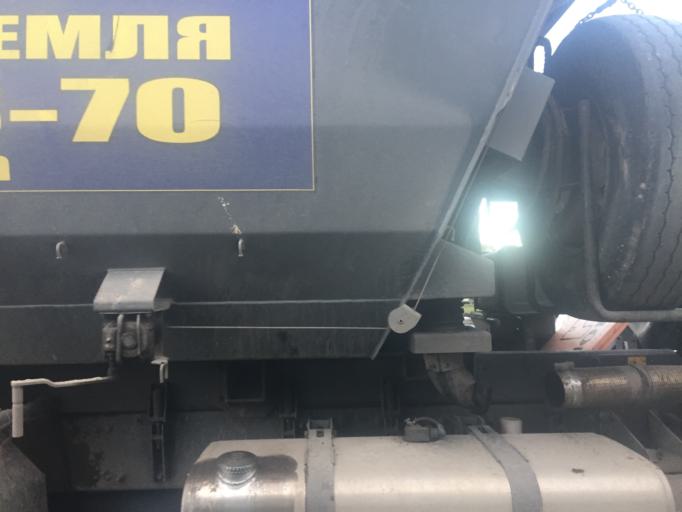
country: RU
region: St.-Petersburg
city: Obukhovo
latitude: 59.8848
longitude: 30.4666
